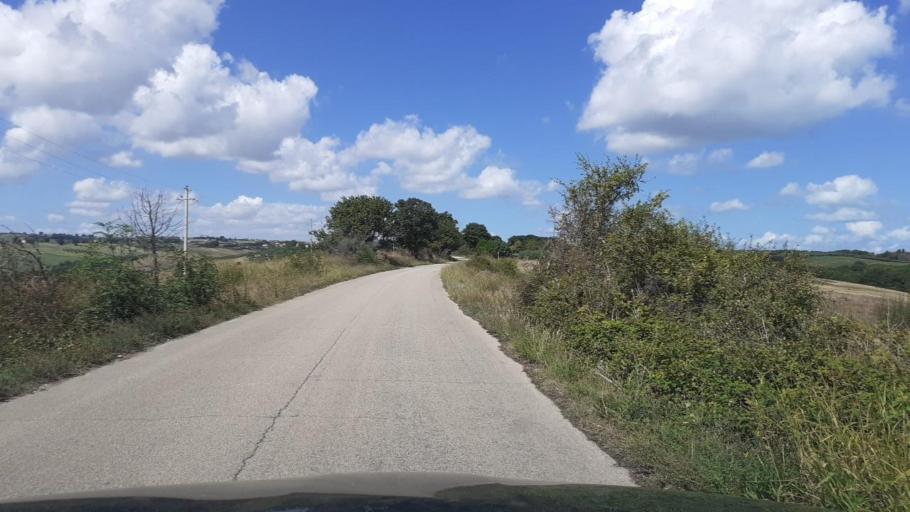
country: IT
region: Molise
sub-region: Provincia di Campobasso
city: Petacciato
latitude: 41.9958
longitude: 14.8991
